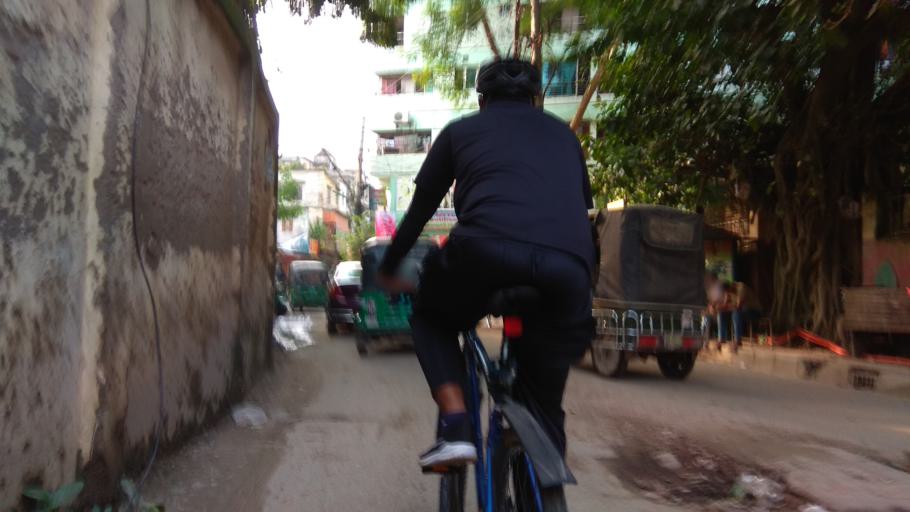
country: BD
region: Dhaka
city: Tungi
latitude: 23.8254
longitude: 90.3943
